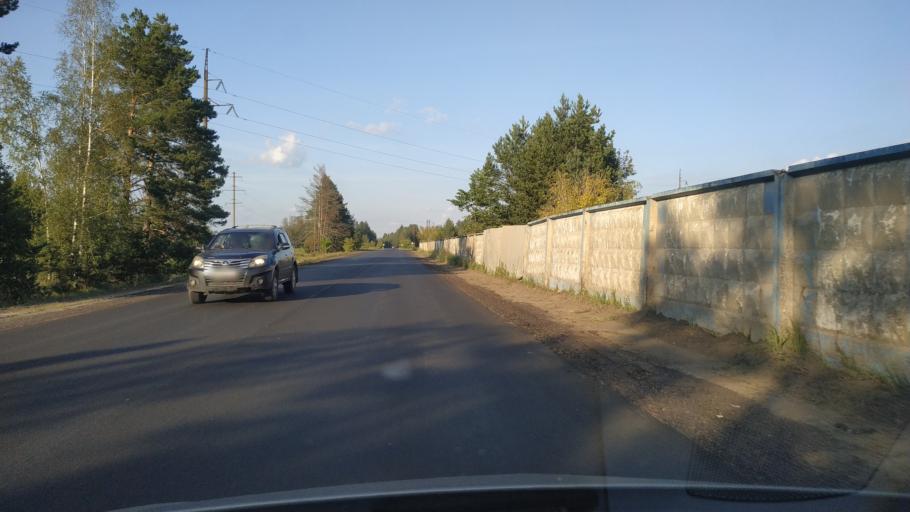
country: RU
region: Moskovskaya
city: Kerva
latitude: 55.5764
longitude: 39.6839
